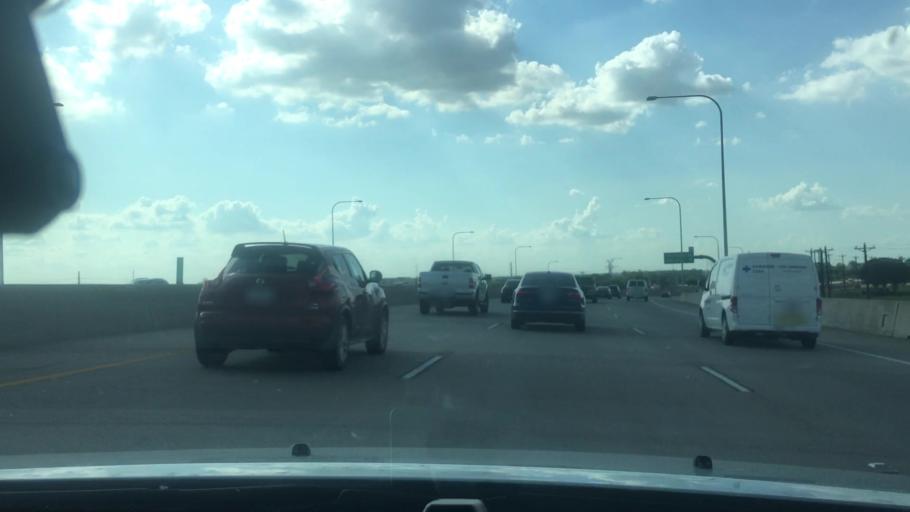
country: US
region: Texas
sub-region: Collin County
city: Frisco
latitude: 33.1380
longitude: -96.8363
